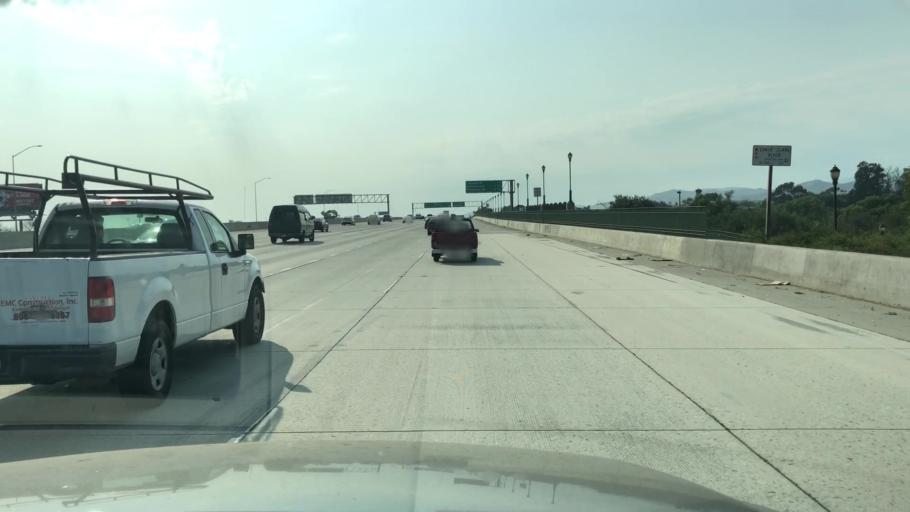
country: US
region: California
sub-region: Ventura County
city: El Rio
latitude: 34.2415
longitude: -119.1862
